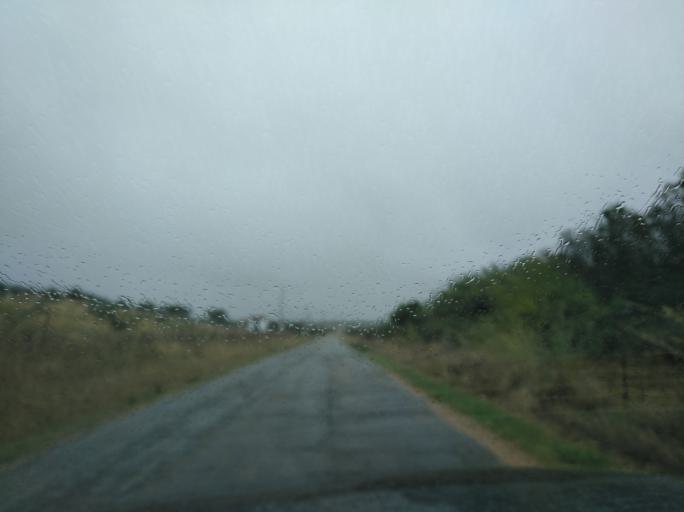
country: PT
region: Portalegre
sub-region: Campo Maior
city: Campo Maior
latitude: 38.9788
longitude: -7.0693
